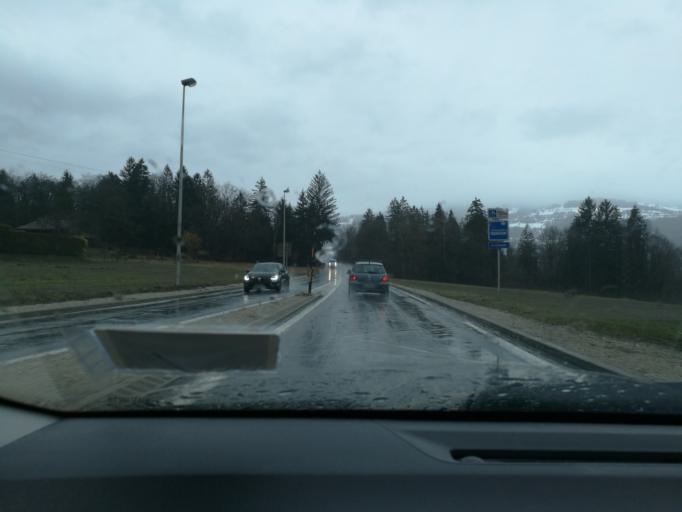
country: FR
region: Rhone-Alpes
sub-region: Departement de la Haute-Savoie
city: Domancy
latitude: 45.9288
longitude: 6.6552
